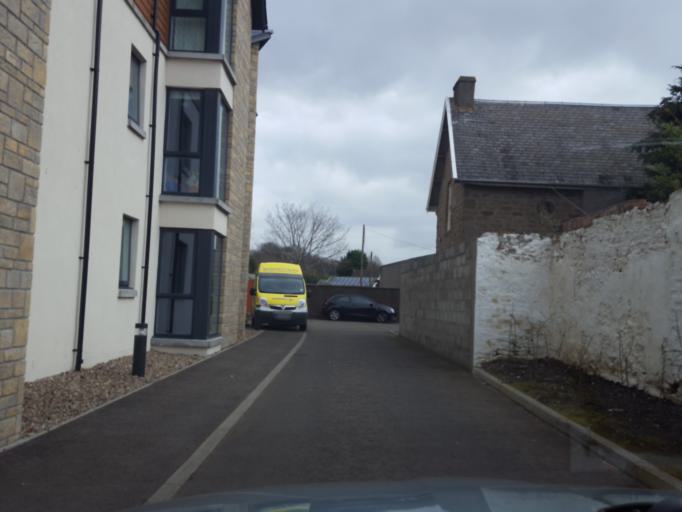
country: GB
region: Scotland
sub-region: Fife
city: Tayport
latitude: 56.4663
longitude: -2.8647
